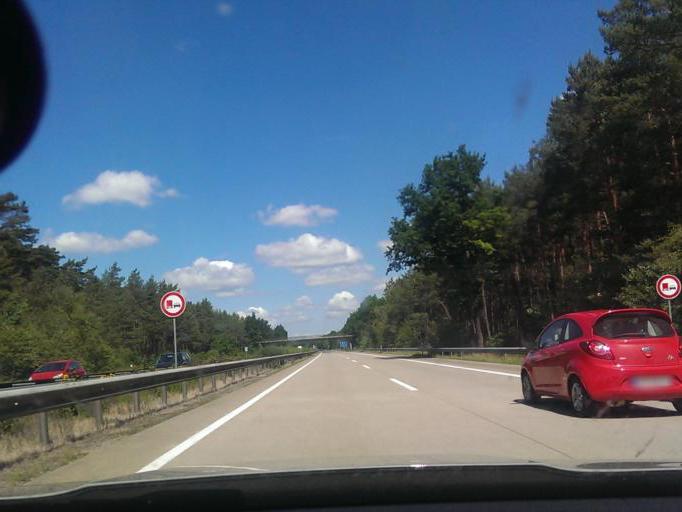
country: DE
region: Lower Saxony
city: Walsrode
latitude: 52.8251
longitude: 9.6088
